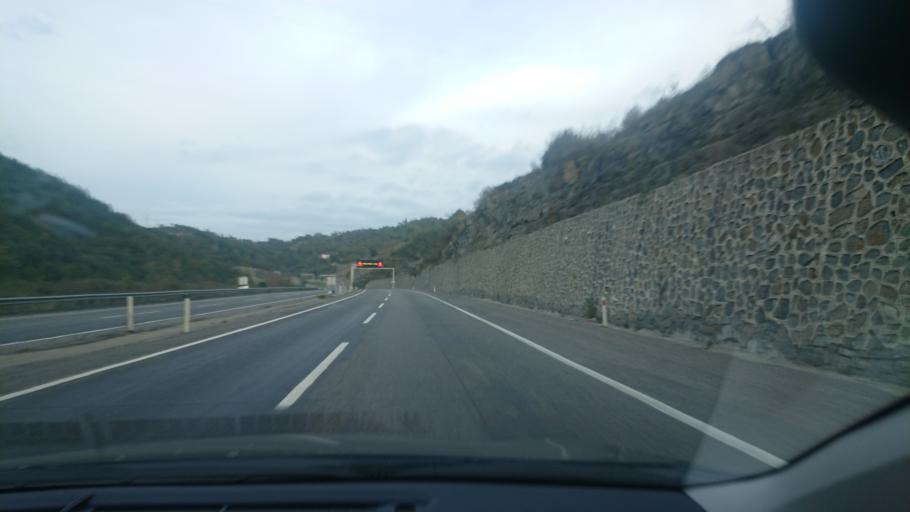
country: TR
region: Zonguldak
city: Beycuma
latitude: 41.4090
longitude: 31.9316
